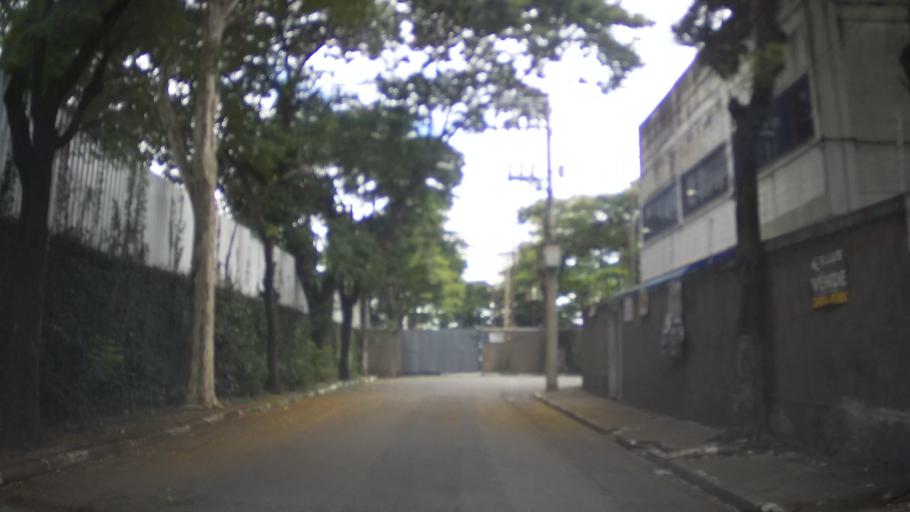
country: BR
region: Sao Paulo
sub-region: Guarulhos
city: Guarulhos
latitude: -23.4945
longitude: -46.5563
